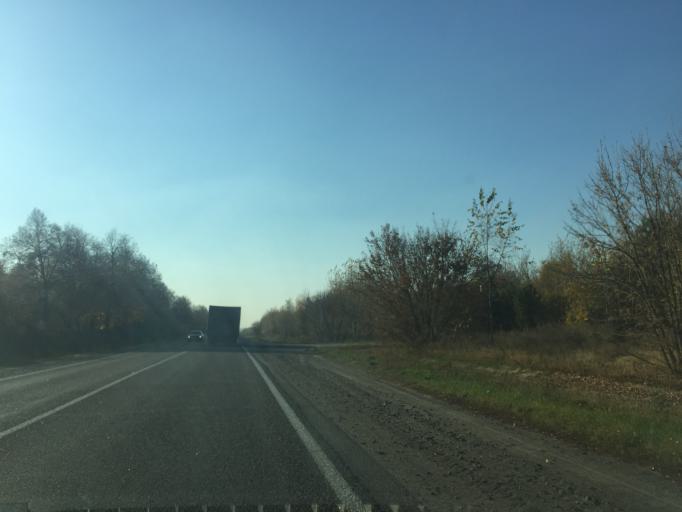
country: BY
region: Gomel
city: Dobrush
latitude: 52.3884
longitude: 31.4545
